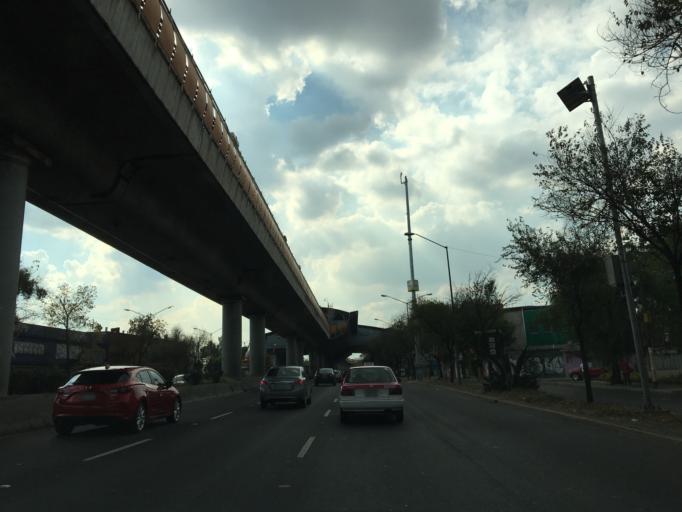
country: MX
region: Mexico City
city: Venustiano Carranza
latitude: 19.4374
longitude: -99.1020
